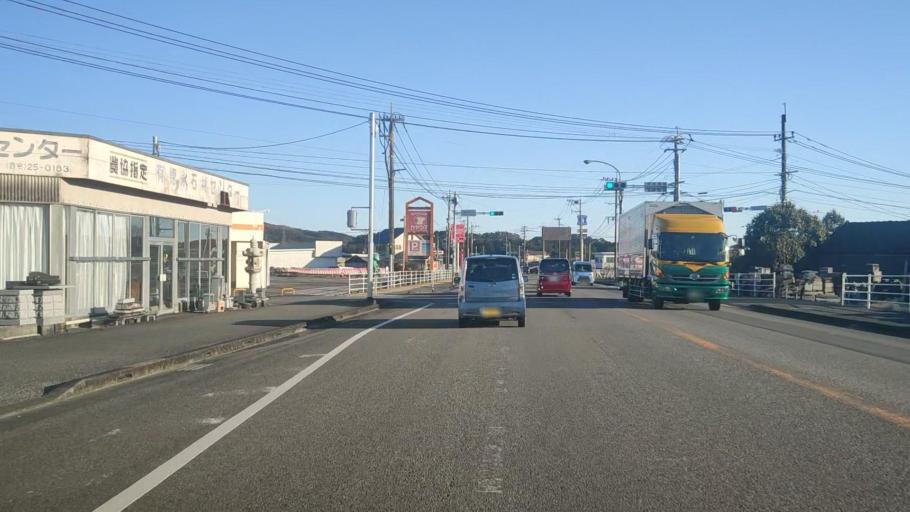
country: JP
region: Miyazaki
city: Takanabe
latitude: 32.2563
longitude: 131.5550
